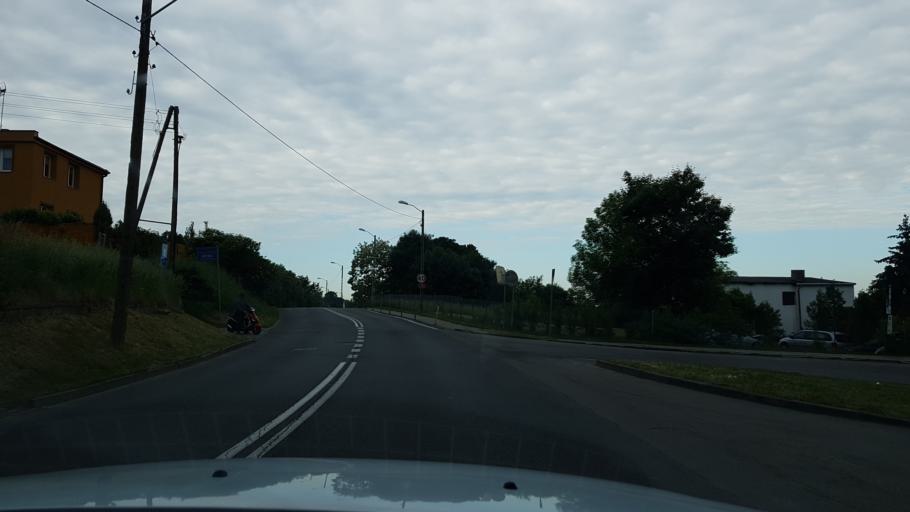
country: PL
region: West Pomeranian Voivodeship
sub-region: Szczecin
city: Szczecin
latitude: 53.3436
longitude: 14.5584
